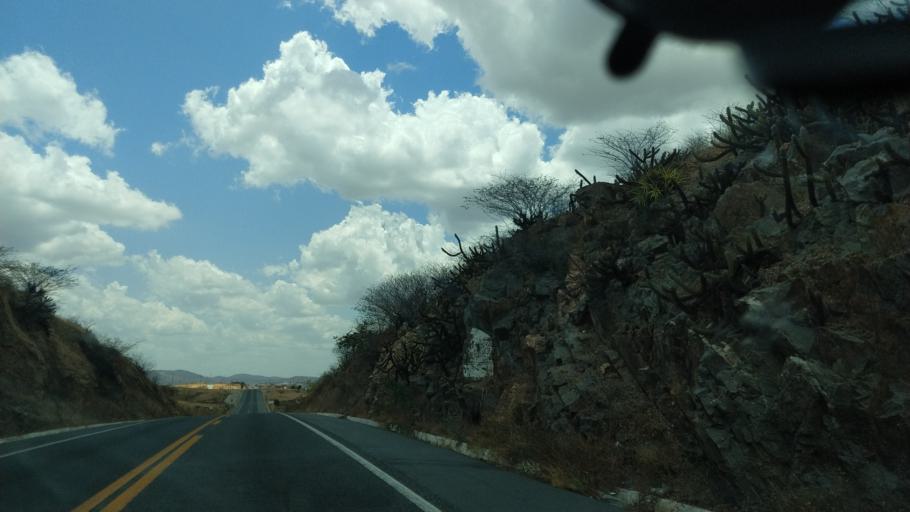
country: BR
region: Rio Grande do Norte
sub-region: Currais Novos
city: Currais Novos
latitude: -6.2564
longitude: -36.4891
